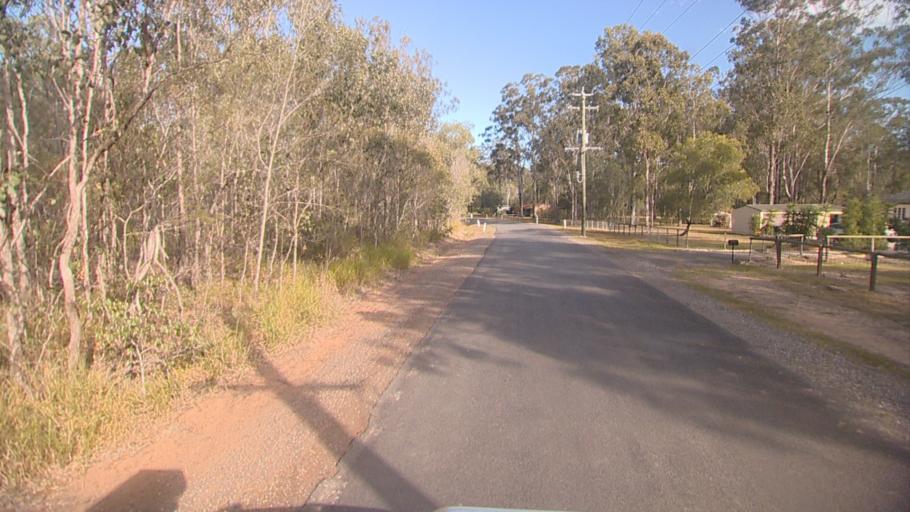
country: AU
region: Queensland
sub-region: Logan
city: Cedar Vale
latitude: -27.8254
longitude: 153.0661
